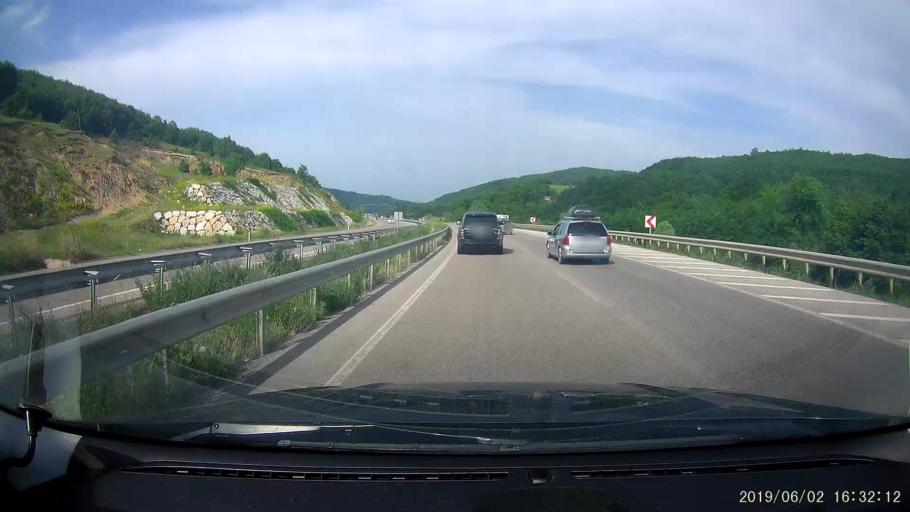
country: TR
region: Samsun
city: Ladik
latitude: 41.0374
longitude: 35.9158
